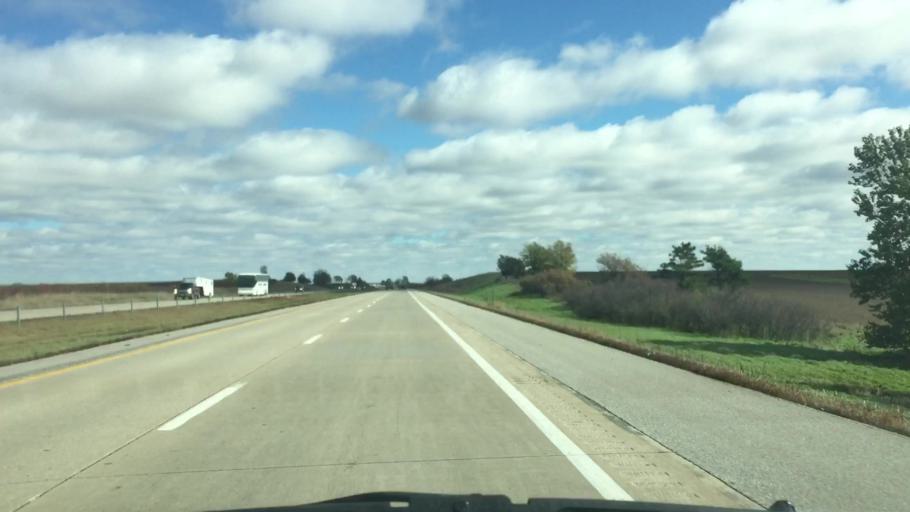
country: US
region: Iowa
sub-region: Poweshiek County
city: Brooklyn
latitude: 41.6956
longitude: -92.5232
